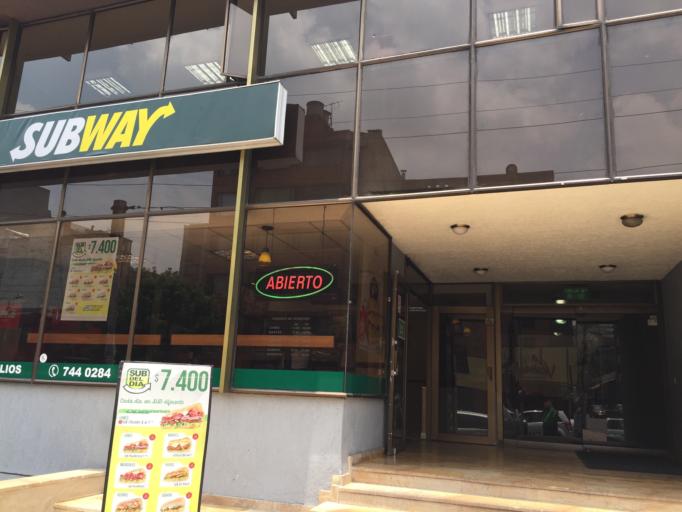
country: CO
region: Bogota D.C.
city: Barrio San Luis
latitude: 4.6514
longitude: -74.0592
